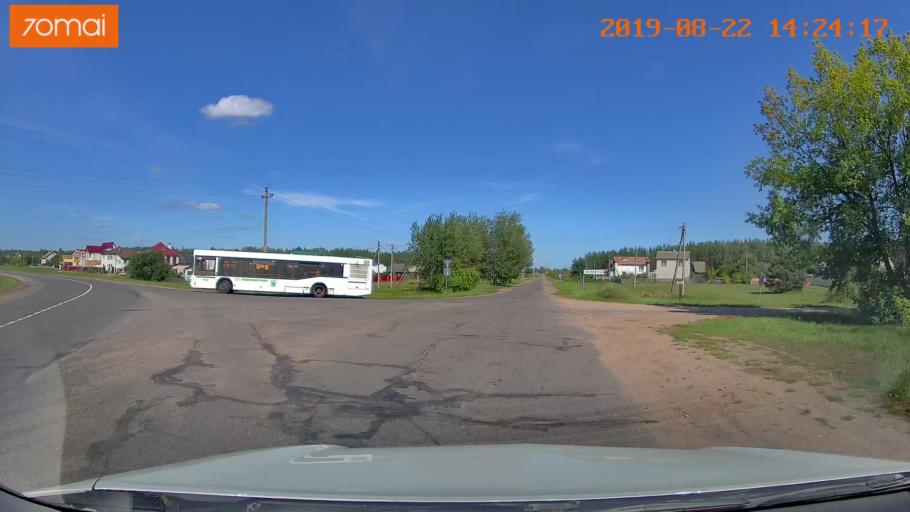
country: BY
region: Mogilev
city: Asipovichy
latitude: 53.2976
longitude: 28.5965
